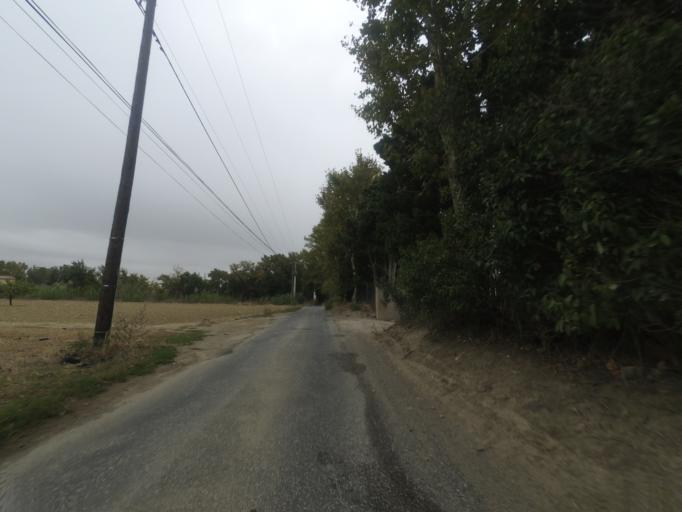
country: FR
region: Languedoc-Roussillon
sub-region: Departement des Pyrenees-Orientales
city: Baho
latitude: 42.6969
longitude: 2.8293
